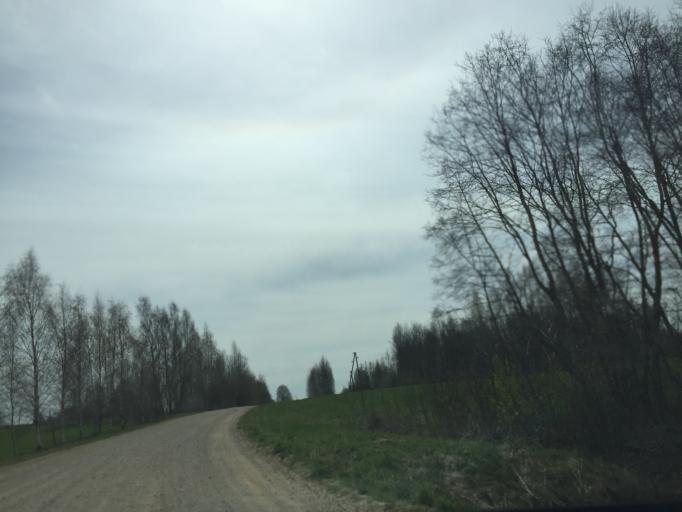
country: LV
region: Ludzas Rajons
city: Ludza
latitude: 56.5795
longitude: 27.5488
